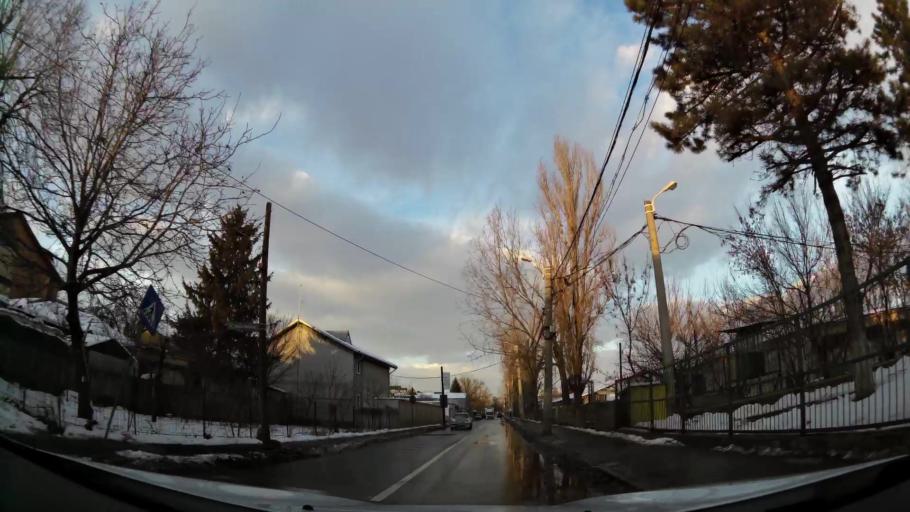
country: RO
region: Ilfov
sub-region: Comuna Popesti-Leordeni
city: Popesti-Leordeni
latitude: 44.3807
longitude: 26.1426
